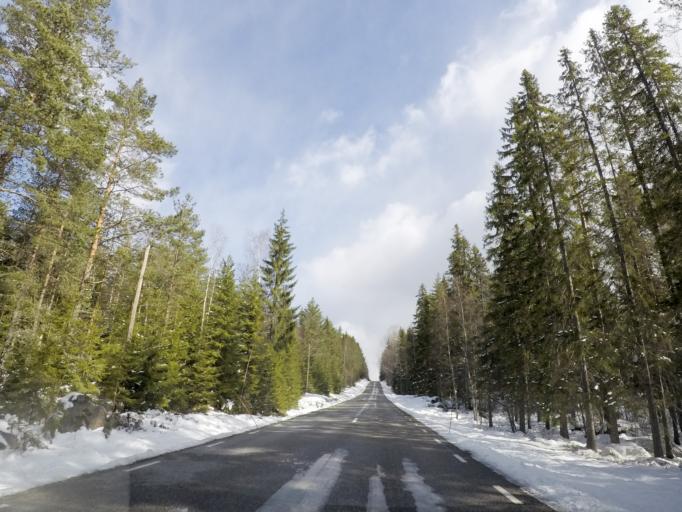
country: SE
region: OErebro
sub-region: Lindesbergs Kommun
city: Stora
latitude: 59.8969
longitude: 15.2287
